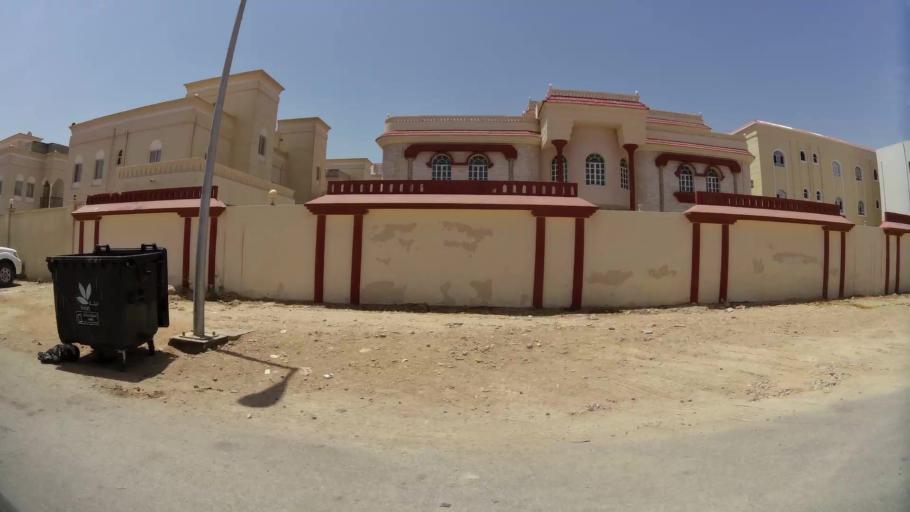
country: OM
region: Zufar
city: Salalah
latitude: 17.0598
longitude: 54.1527
